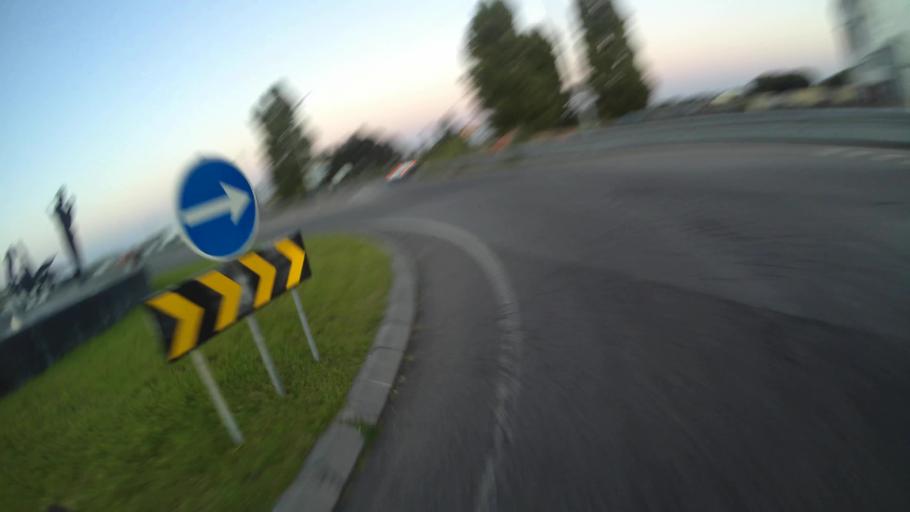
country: PT
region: Aveiro
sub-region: Ilhavo
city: Gafanha da Nazare
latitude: 40.6304
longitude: -8.6888
